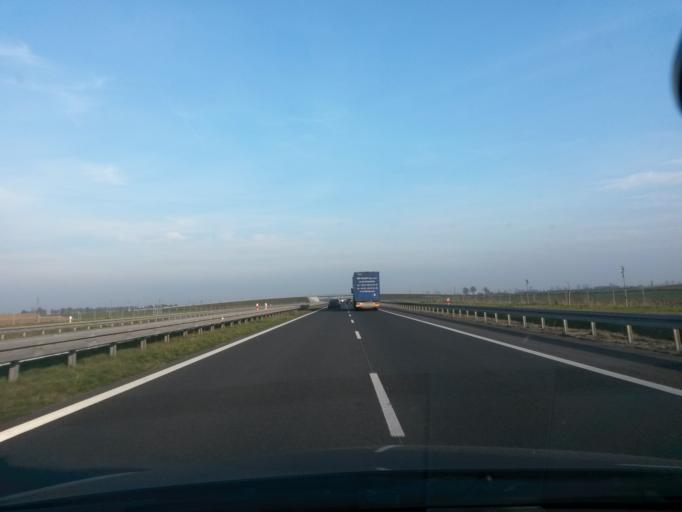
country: PL
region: Lower Silesian Voivodeship
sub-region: Powiat olesnicki
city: Dobroszyce
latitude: 51.2237
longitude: 17.3406
